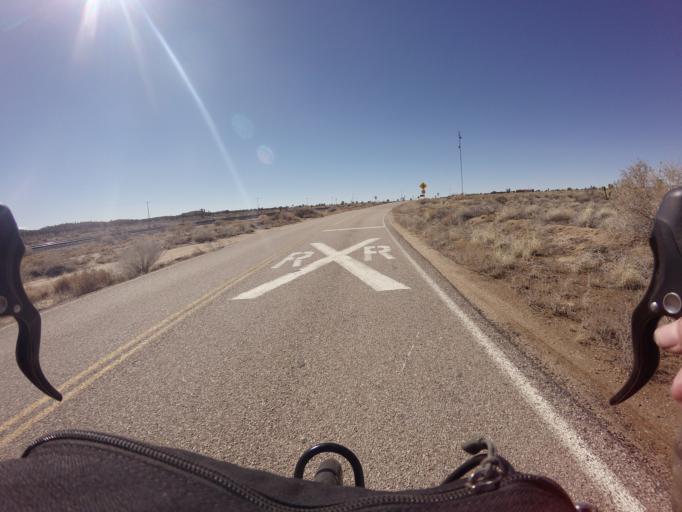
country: US
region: Nevada
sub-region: Clark County
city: Sandy Valley
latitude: 35.2376
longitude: -115.4991
